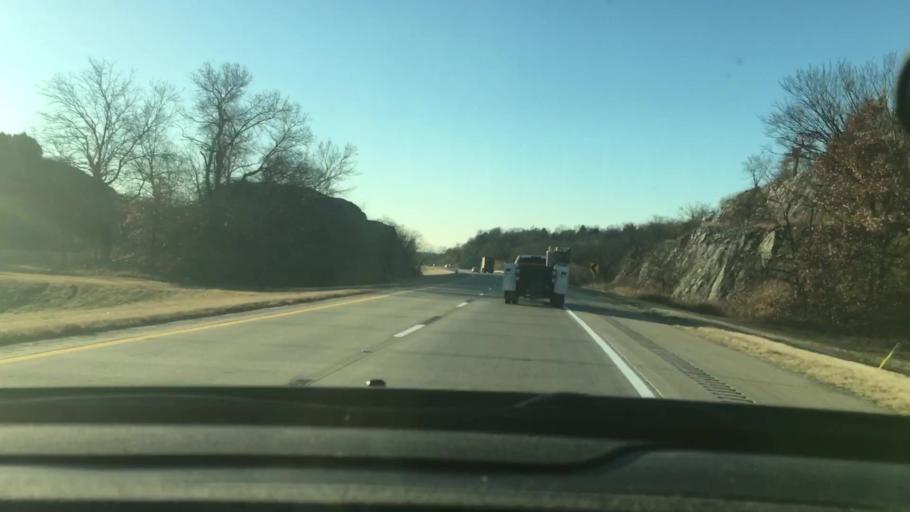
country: US
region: Oklahoma
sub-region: Murray County
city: Davis
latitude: 34.3569
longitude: -97.1492
